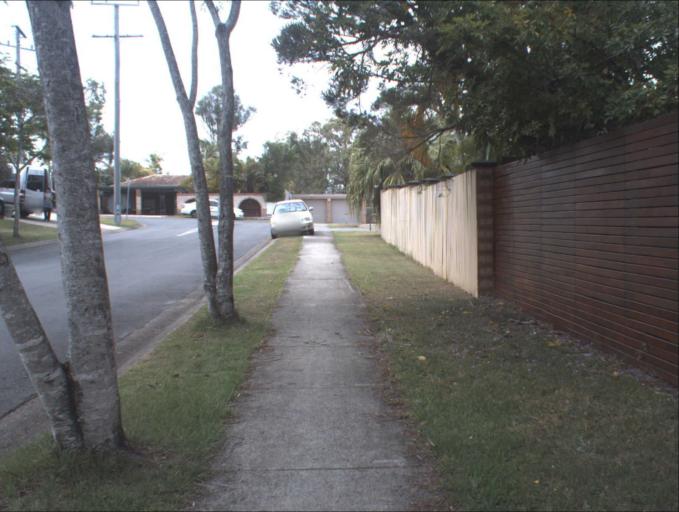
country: AU
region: Queensland
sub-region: Logan
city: Slacks Creek
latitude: -27.6310
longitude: 153.1422
